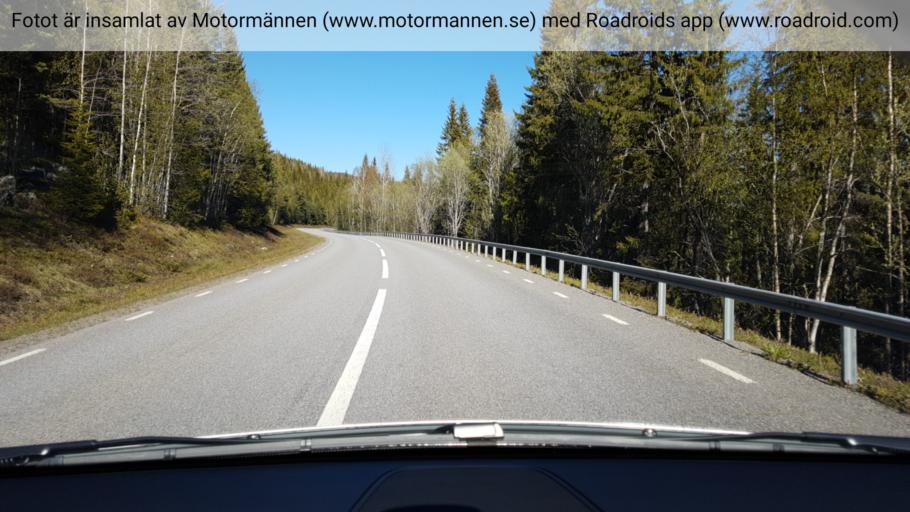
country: SE
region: Jaemtland
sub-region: Stroemsunds Kommun
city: Stroemsund
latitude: 64.3378
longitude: 14.9071
